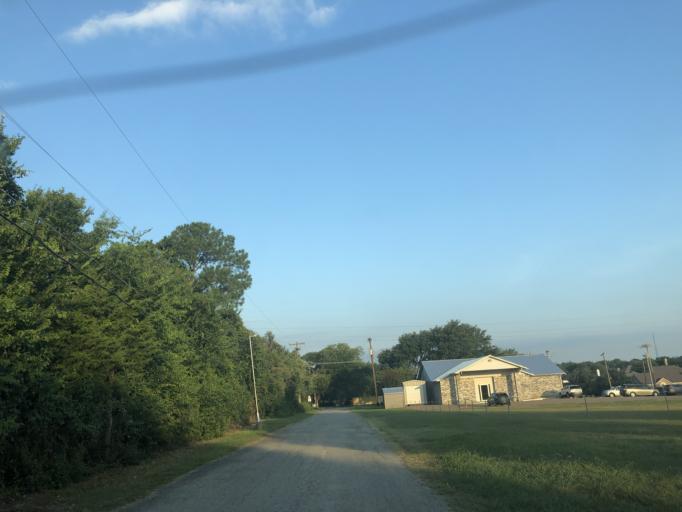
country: US
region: Texas
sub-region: Dallas County
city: Sunnyvale
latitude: 32.8392
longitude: -96.5682
